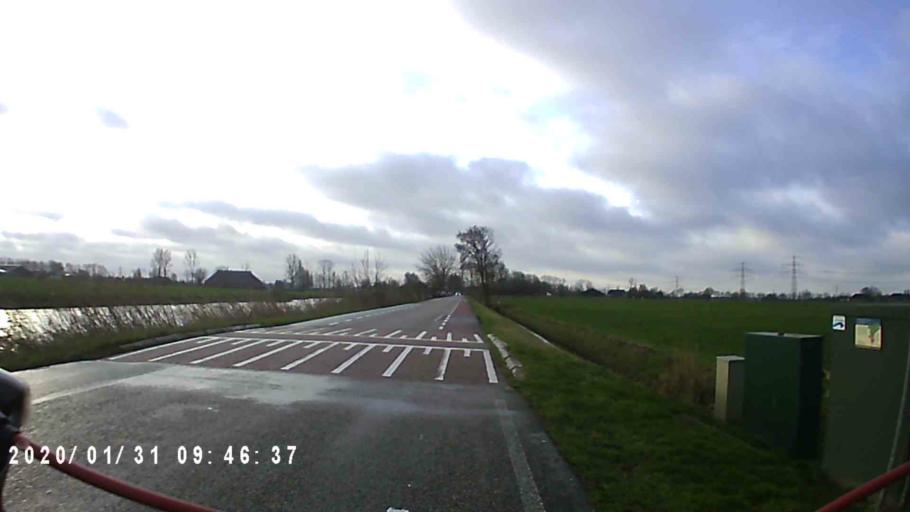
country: NL
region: Groningen
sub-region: Gemeente Zuidhorn
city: Aduard
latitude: 53.2656
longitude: 6.4831
